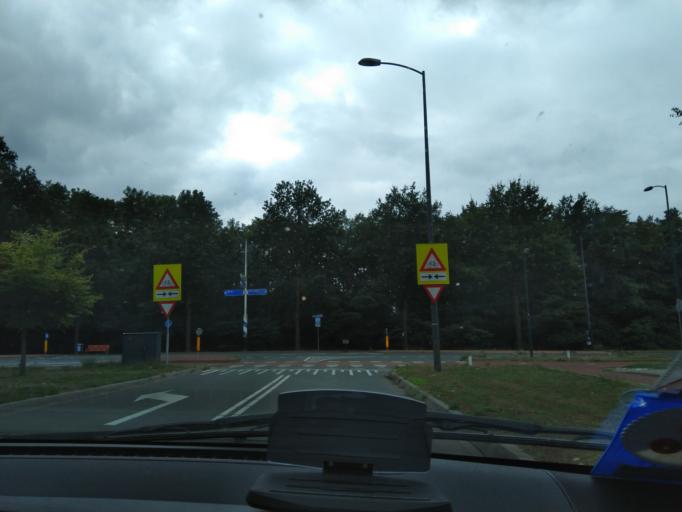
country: NL
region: North Brabant
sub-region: Gemeente Oosterhout
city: Oosterhout
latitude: 51.6216
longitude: 4.8504
